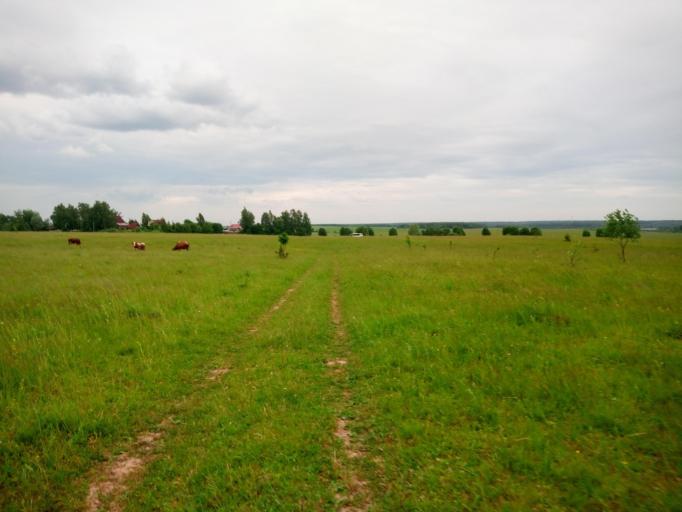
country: RU
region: Moskovskaya
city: Vereya
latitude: 55.1555
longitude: 36.0609
